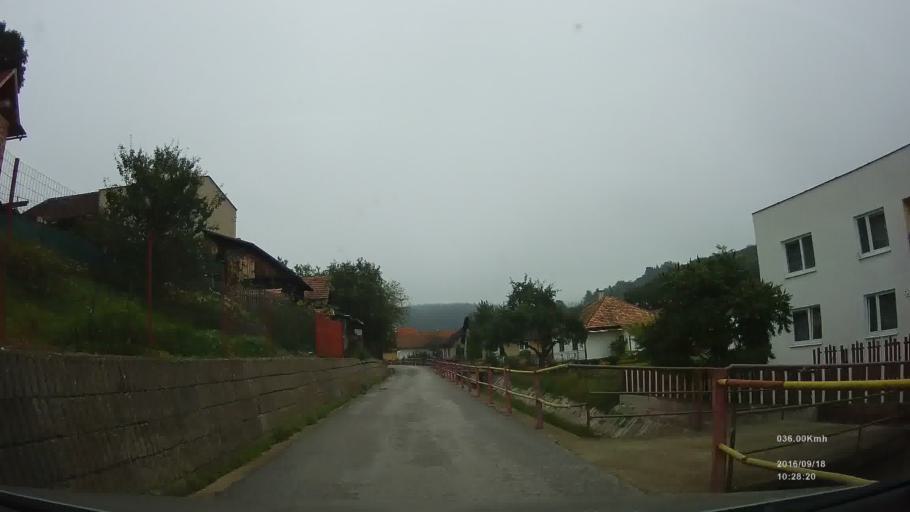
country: SK
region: Kosicky
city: Spisska Nova Ves
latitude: 48.9493
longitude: 20.6196
